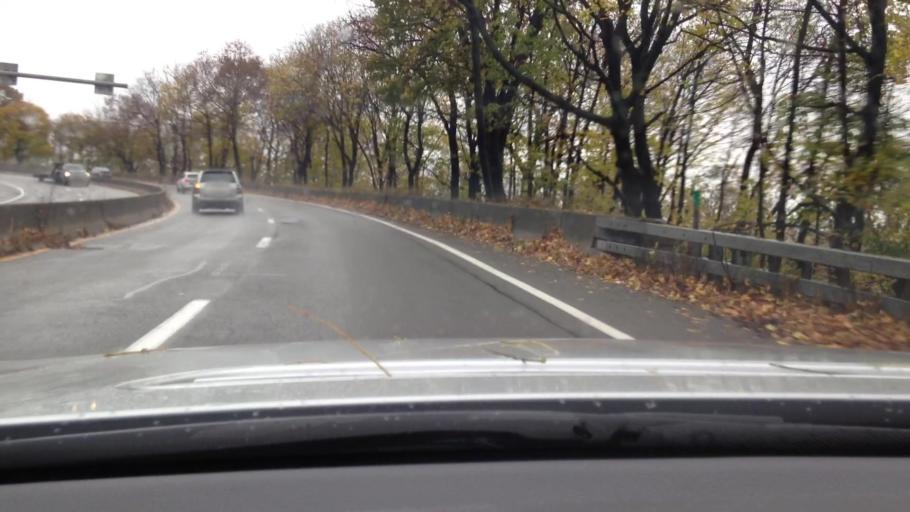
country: US
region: New York
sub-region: Westchester County
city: Peekskill
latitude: 41.2951
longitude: -73.9346
